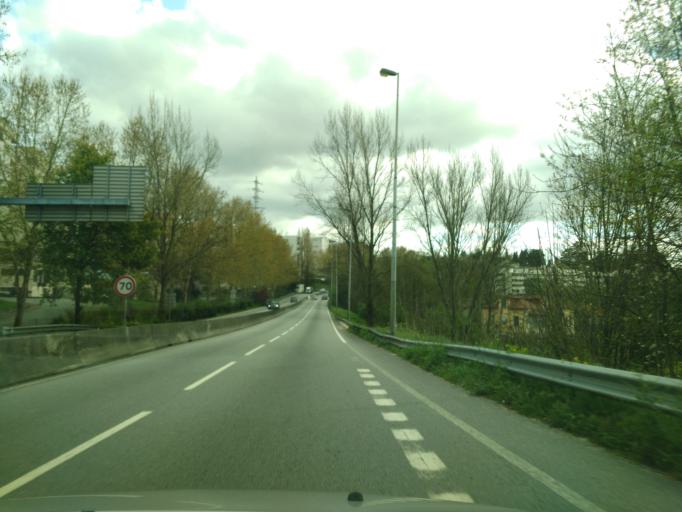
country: PT
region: Braga
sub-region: Guimaraes
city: Guimaraes
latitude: 41.4491
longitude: -8.3071
